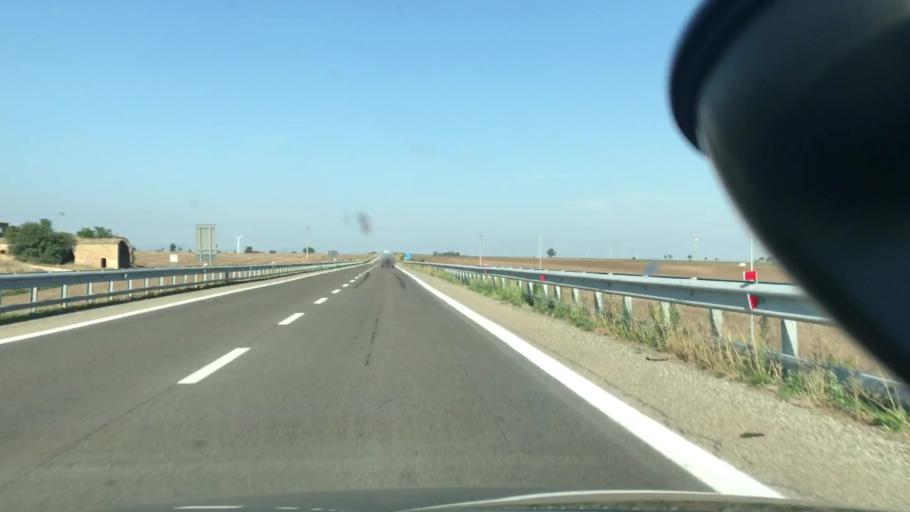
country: IT
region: Basilicate
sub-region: Provincia di Potenza
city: Montemilone
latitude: 40.9878
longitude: 15.9086
